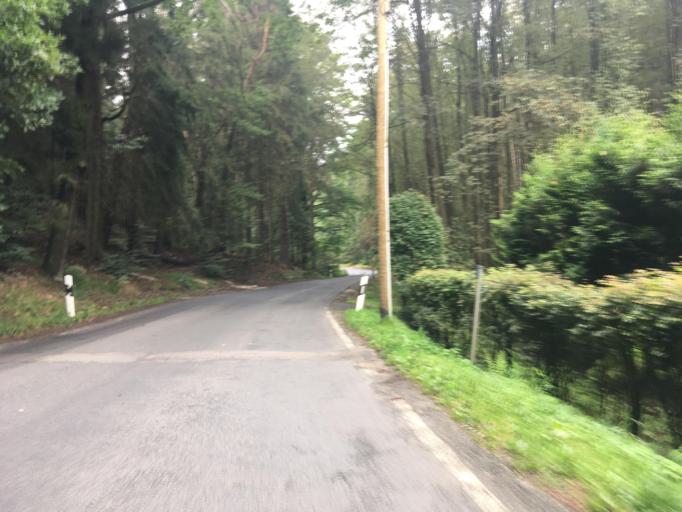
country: DE
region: Saxony
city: Bad Schandau
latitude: 50.9197
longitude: 14.1907
